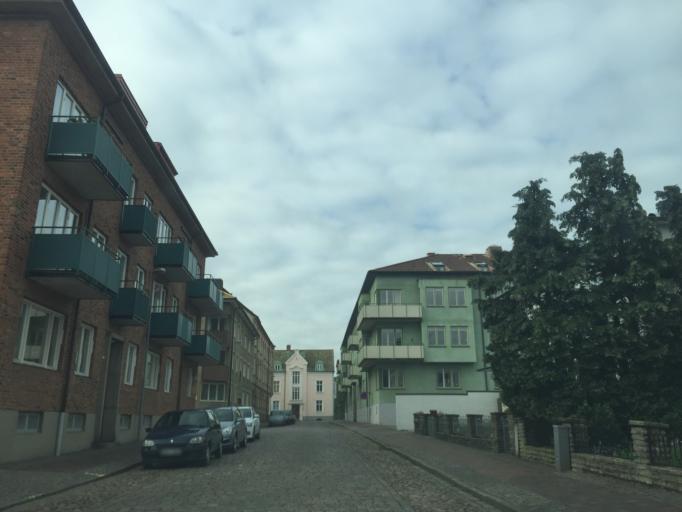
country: SE
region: Skane
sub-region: Angelholms Kommun
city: AEngelholm
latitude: 56.2446
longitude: 12.8577
